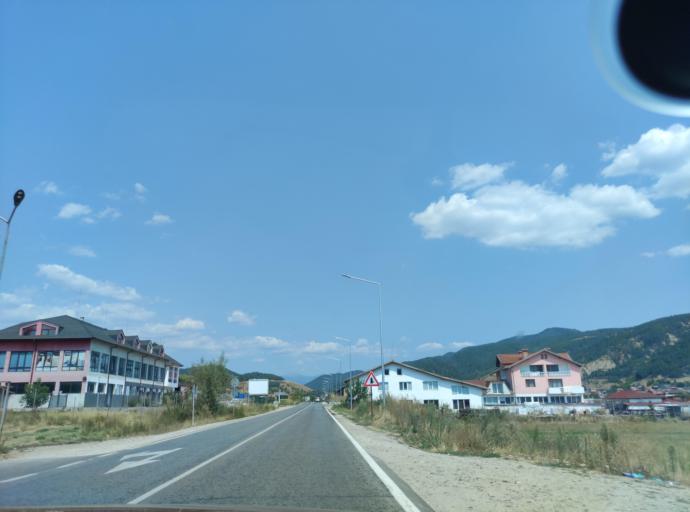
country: BG
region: Blagoevgrad
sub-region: Obshtina Belitsa
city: Belitsa
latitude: 41.9145
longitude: 23.5784
